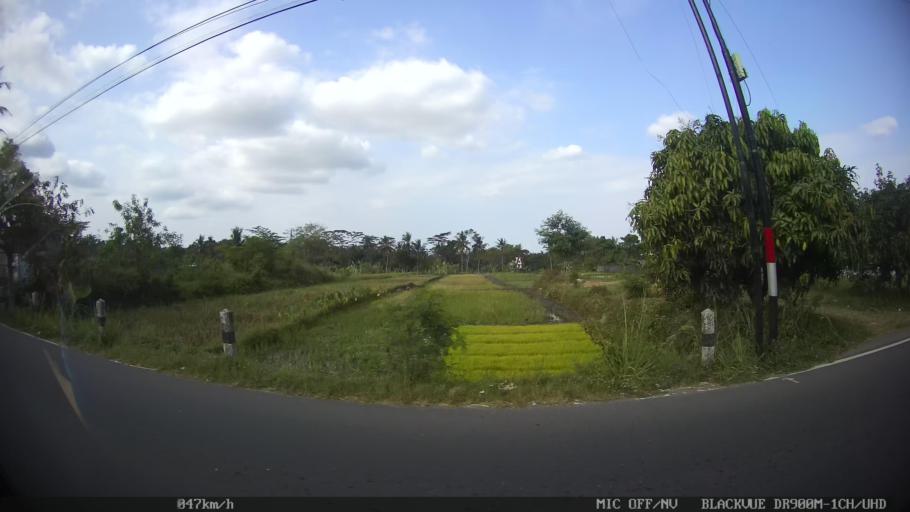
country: ID
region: Central Java
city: Candi Prambanan
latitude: -7.7039
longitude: 110.4690
